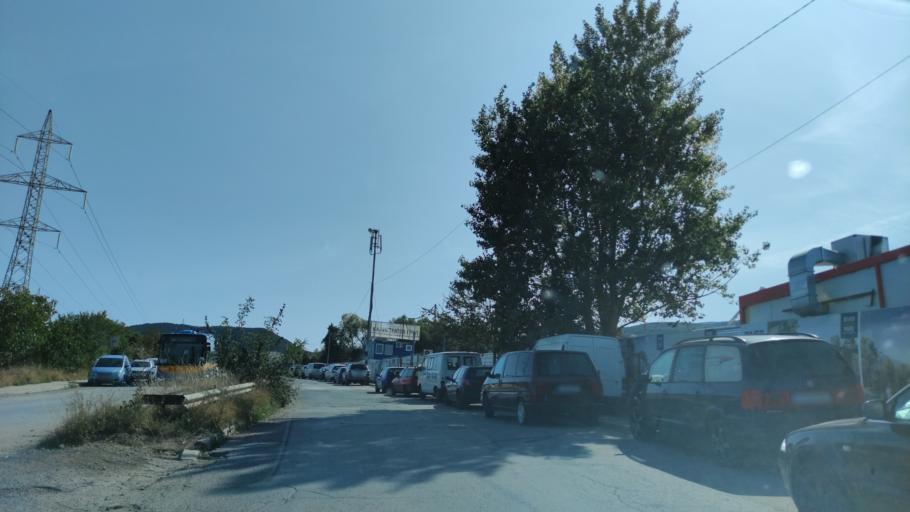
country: BG
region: Sofia-Capital
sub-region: Stolichna Obshtina
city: Sofia
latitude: 42.6215
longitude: 23.3483
